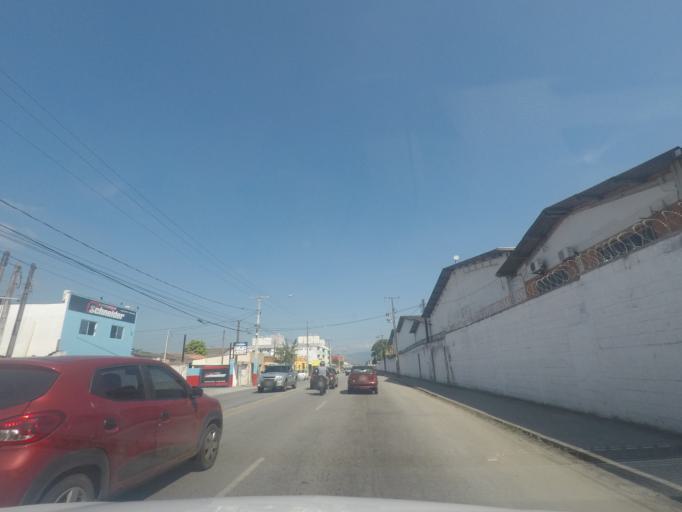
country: BR
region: Parana
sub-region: Paranagua
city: Paranagua
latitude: -25.5442
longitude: -48.5397
